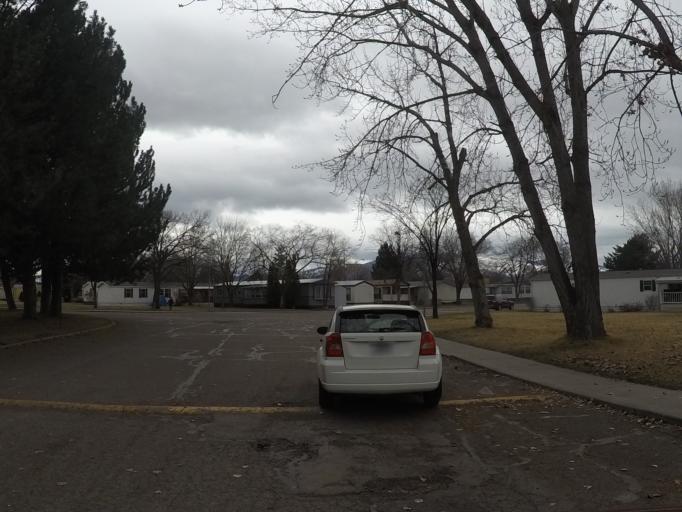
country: US
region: Montana
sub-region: Missoula County
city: Missoula
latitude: 46.8874
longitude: -114.0216
